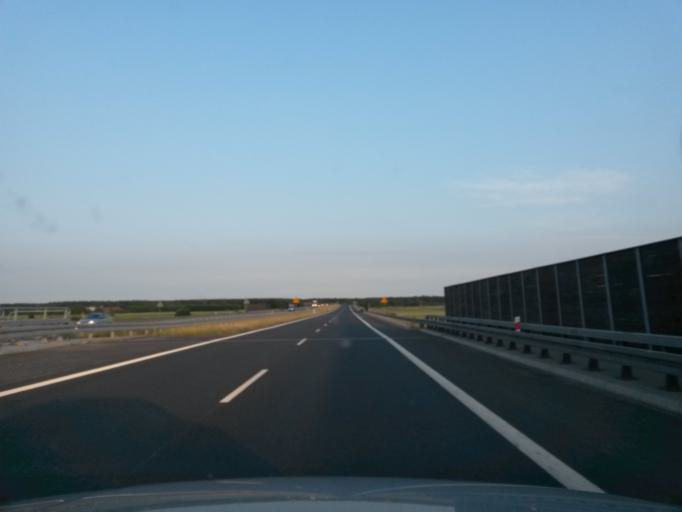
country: PL
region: Lodz Voivodeship
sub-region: Powiat wieruszowski
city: Wieruszow
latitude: 51.3218
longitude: 18.1594
